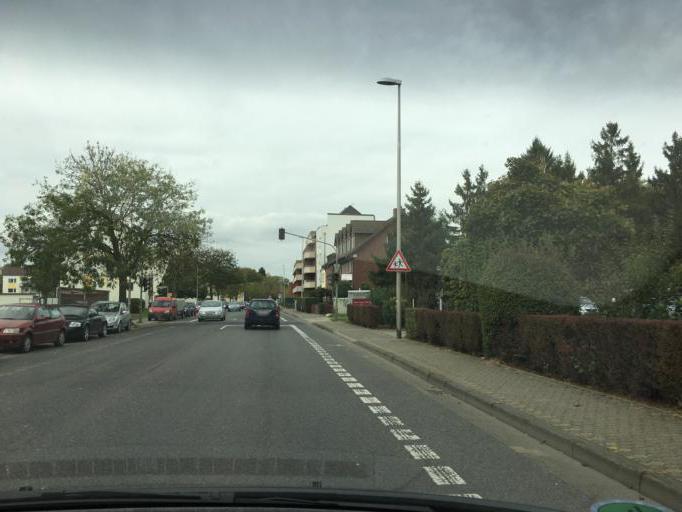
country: DE
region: North Rhine-Westphalia
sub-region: Regierungsbezirk Koln
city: Dueren
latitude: 50.7933
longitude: 6.4829
